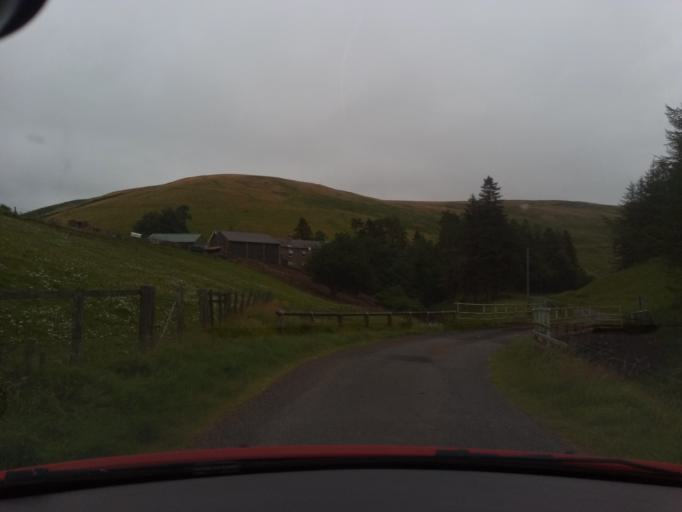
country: GB
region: England
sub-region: Northumberland
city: Rochester
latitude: 55.3972
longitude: -2.2574
